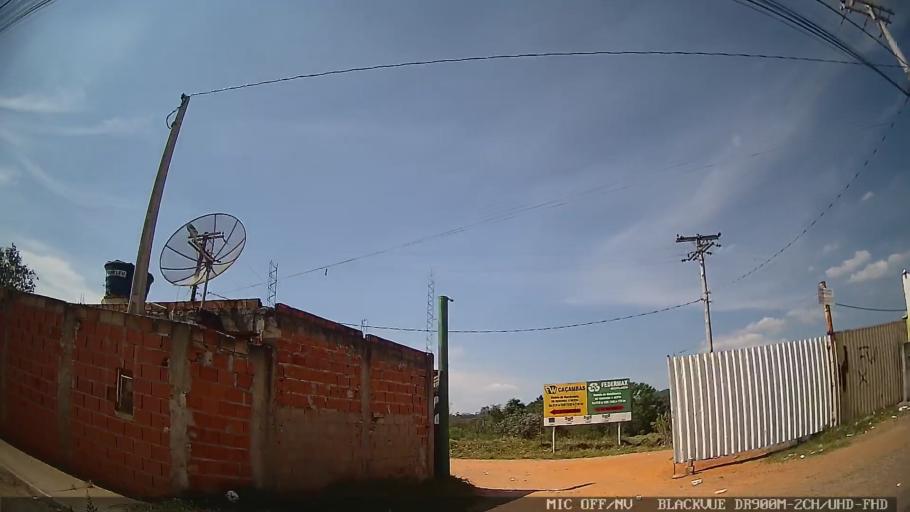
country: BR
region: Sao Paulo
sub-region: Cabreuva
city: Cabreuva
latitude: -23.2697
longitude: -47.0503
